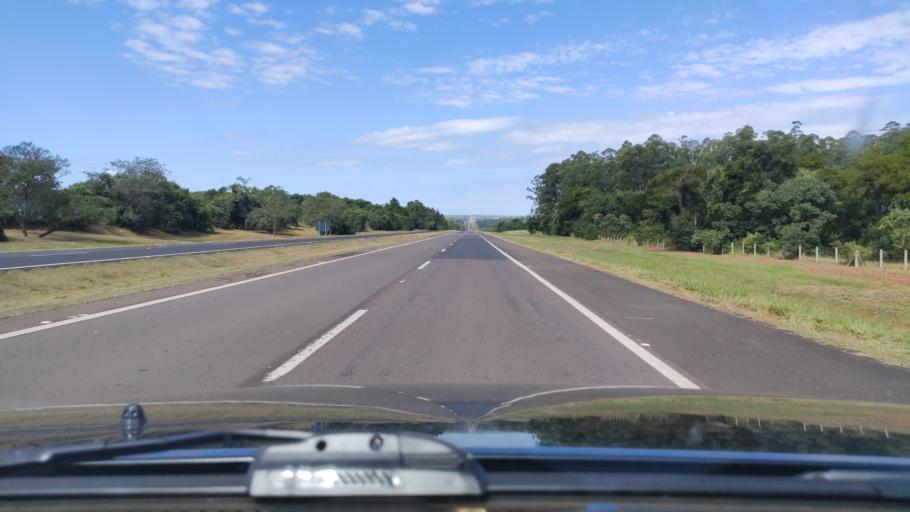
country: BR
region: Sao Paulo
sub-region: Rancharia
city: Rancharia
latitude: -22.4652
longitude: -50.9574
